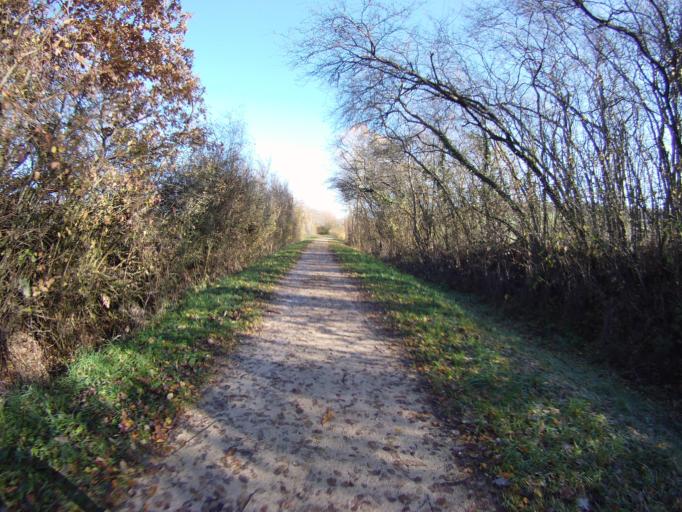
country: FR
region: Lorraine
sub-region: Departement de Meurthe-et-Moselle
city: Faulx
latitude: 48.7917
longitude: 6.2271
